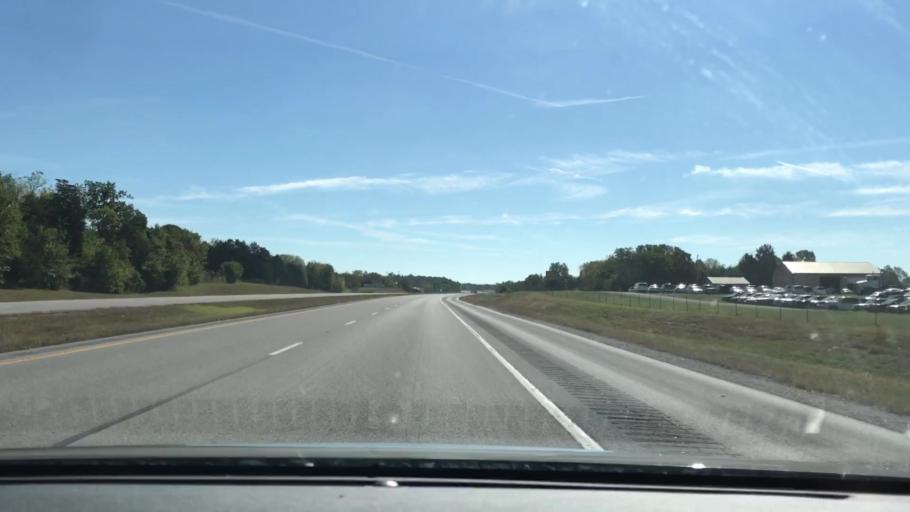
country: US
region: Kentucky
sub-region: Todd County
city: Elkton
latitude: 36.8357
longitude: -87.2367
